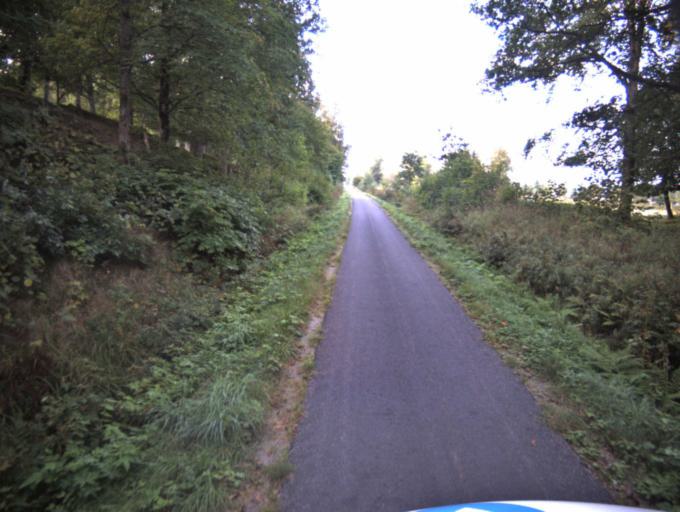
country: SE
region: Vaestra Goetaland
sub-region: Ulricehamns Kommun
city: Ulricehamn
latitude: 57.7249
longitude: 13.4055
